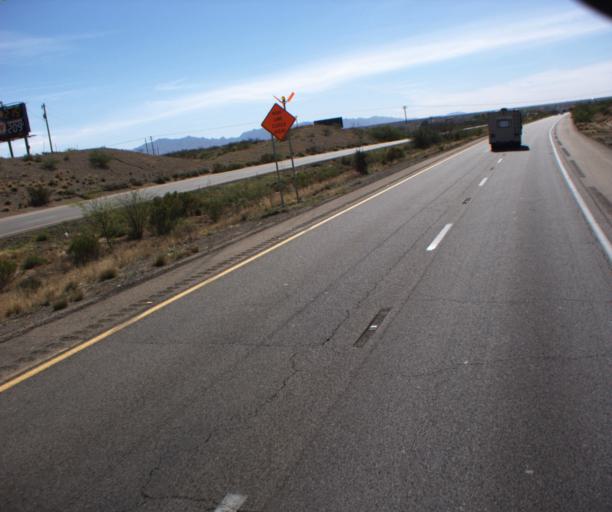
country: US
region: Arizona
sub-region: Cochise County
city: Benson
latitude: 31.9759
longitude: -110.2899
